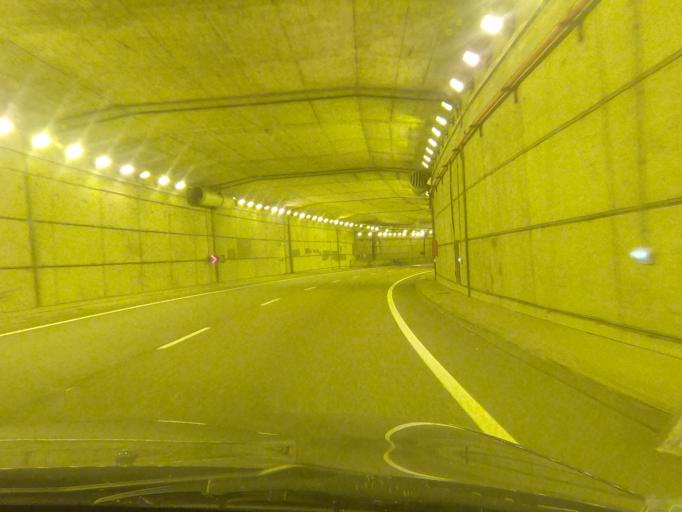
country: ES
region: Galicia
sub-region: Provincia de Pontevedra
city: Vigo
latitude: 42.2392
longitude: -8.7071
